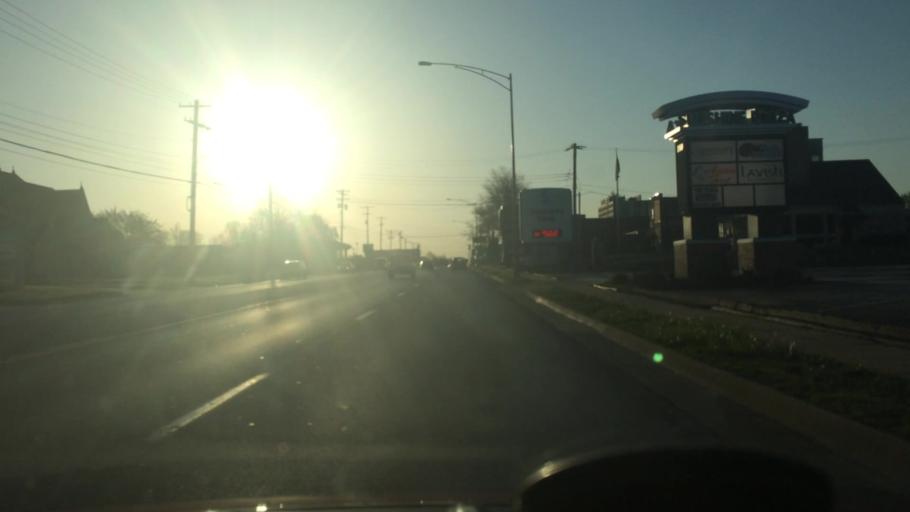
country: US
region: Missouri
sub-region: Greene County
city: Springfield
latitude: 37.1817
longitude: -93.2692
